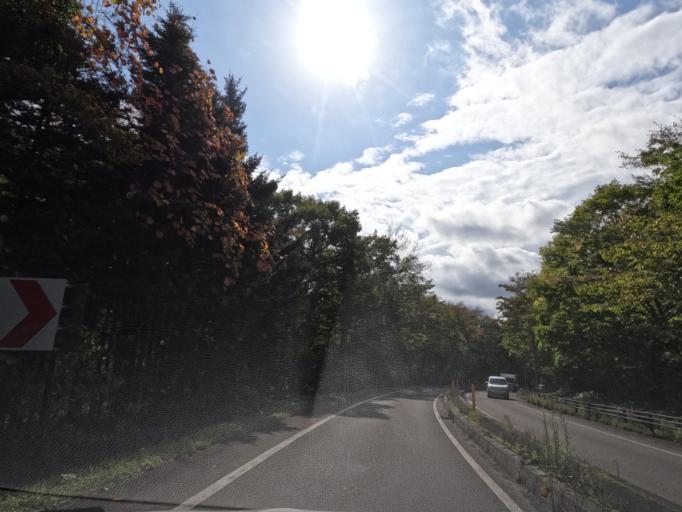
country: JP
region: Hokkaido
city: Chitose
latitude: 42.7974
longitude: 141.5671
